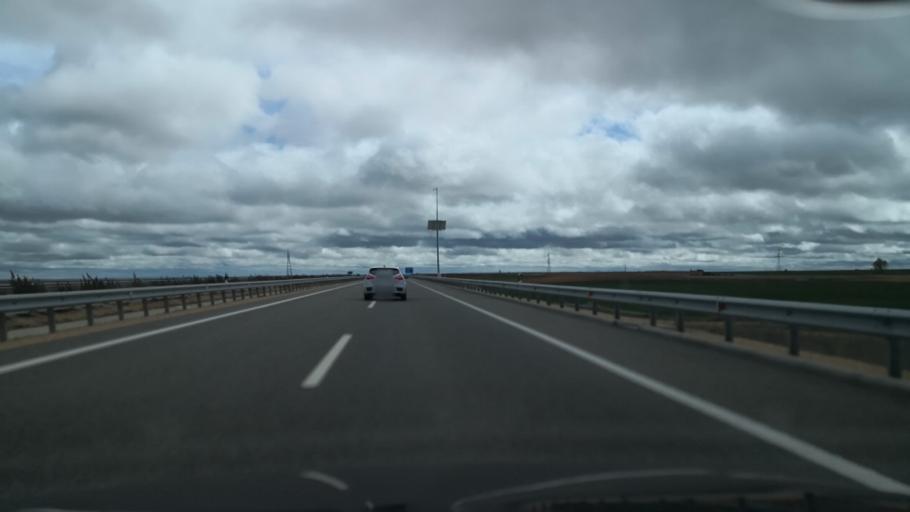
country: ES
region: Castille and Leon
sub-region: Provincia de Zamora
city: Roales
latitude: 41.5897
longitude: -5.7791
